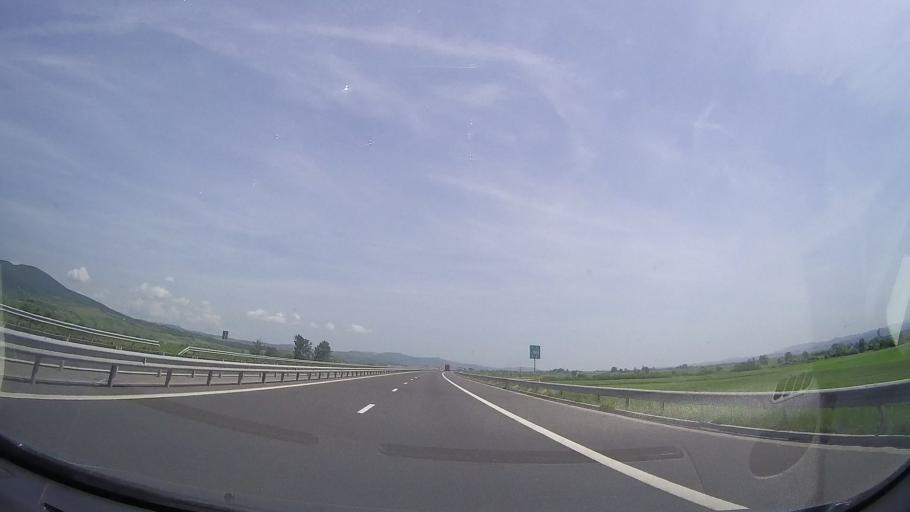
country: RO
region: Hunedoara
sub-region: Comuna Turdas
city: Pricaz
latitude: 45.8674
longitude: 23.1572
